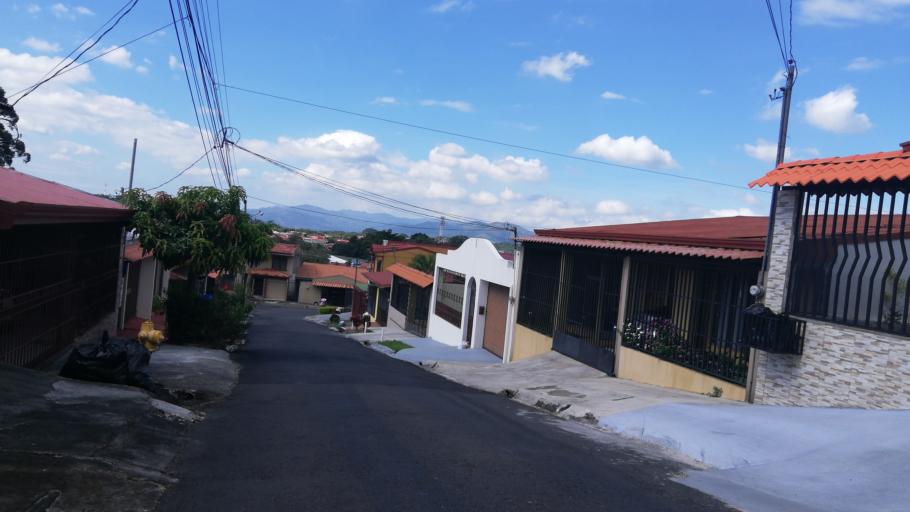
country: CR
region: Alajuela
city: San Juan
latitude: 10.0789
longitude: -84.3104
